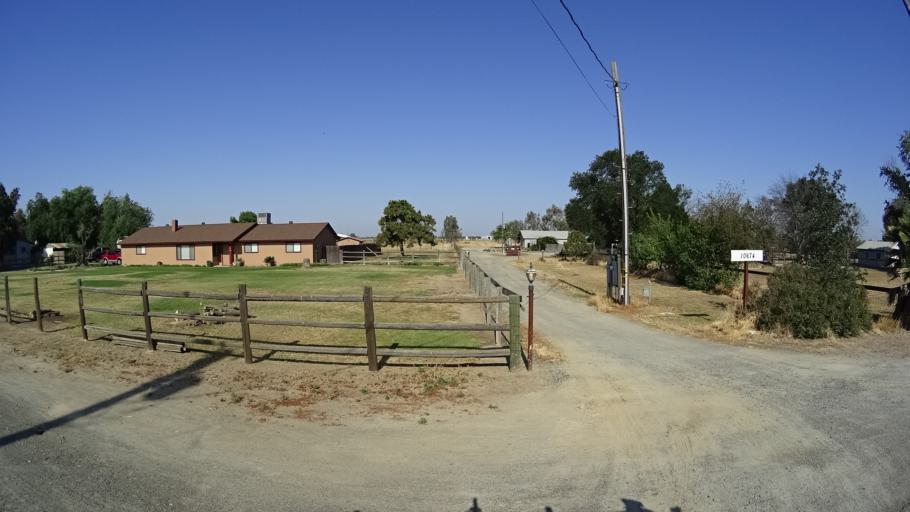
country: US
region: California
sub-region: Kings County
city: Home Garden
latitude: 36.3182
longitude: -119.5831
